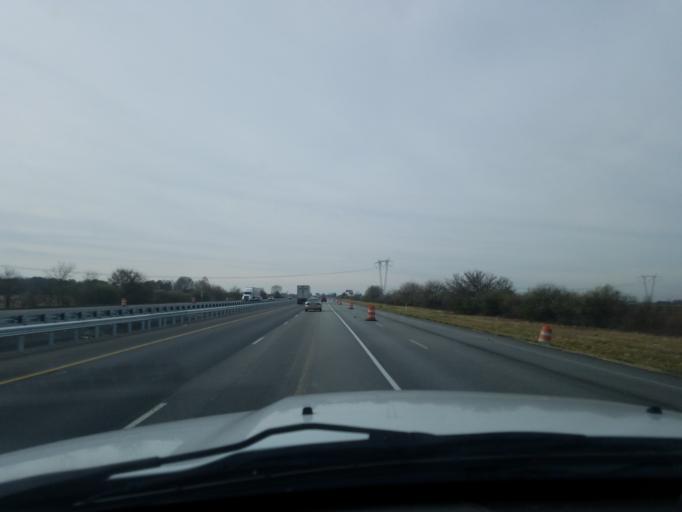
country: US
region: Indiana
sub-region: Madison County
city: Ingalls
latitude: 39.9916
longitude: -85.8081
